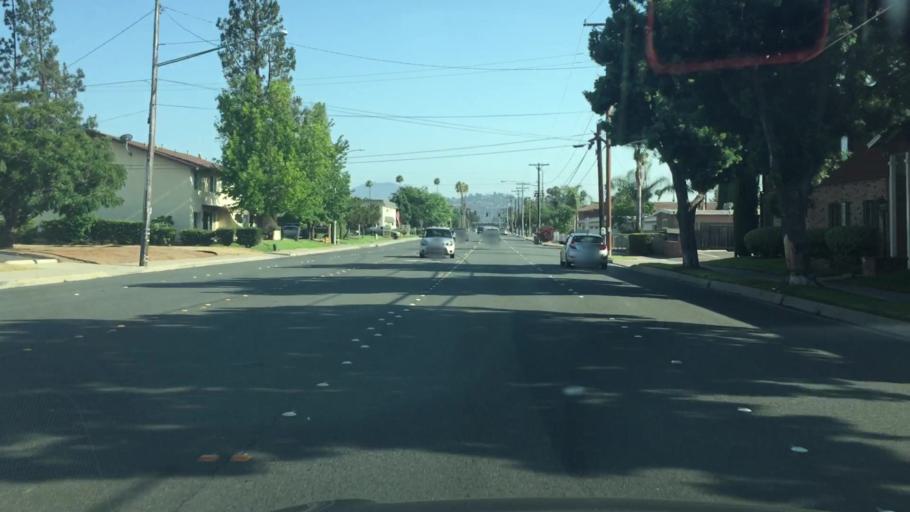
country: US
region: California
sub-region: San Diego County
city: Bostonia
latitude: 32.8103
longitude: -116.9510
